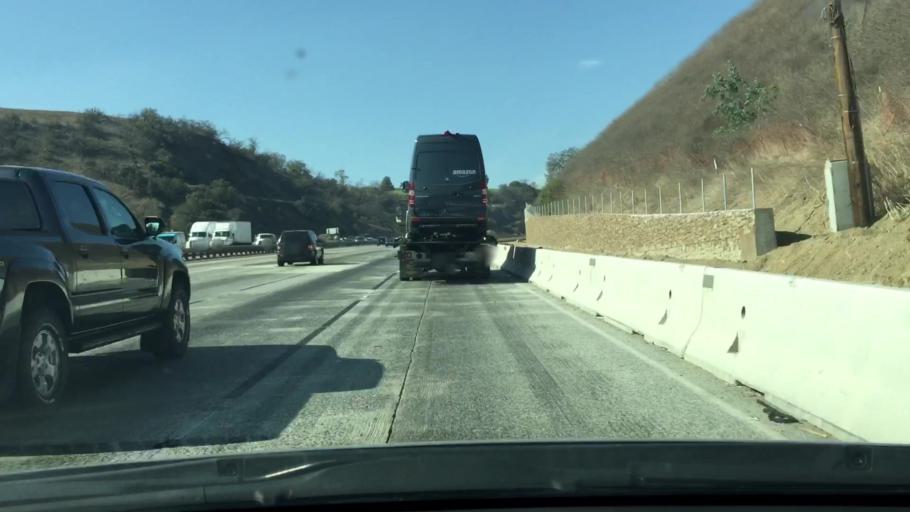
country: US
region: California
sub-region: Los Angeles County
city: Diamond Bar
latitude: 34.0641
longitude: -117.8245
